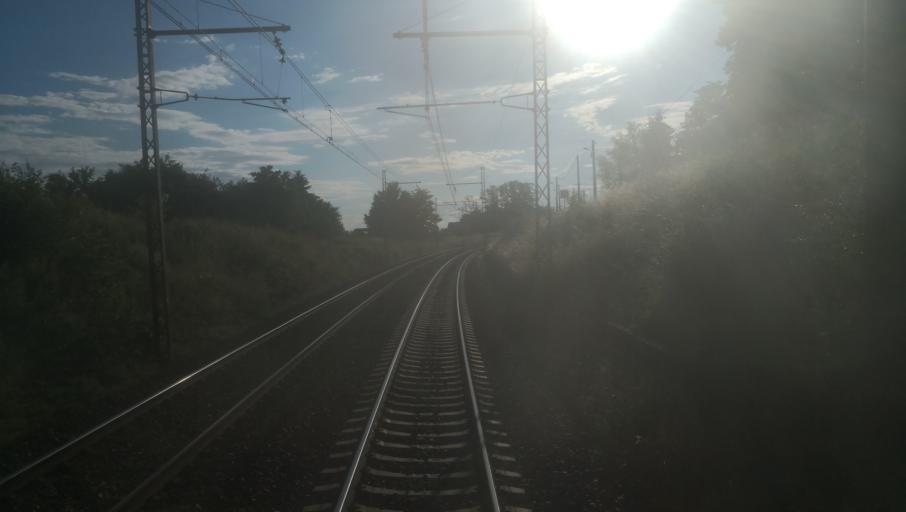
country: FR
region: Centre
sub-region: Departement du Cher
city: Vierzon
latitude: 47.2213
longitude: 2.0799
